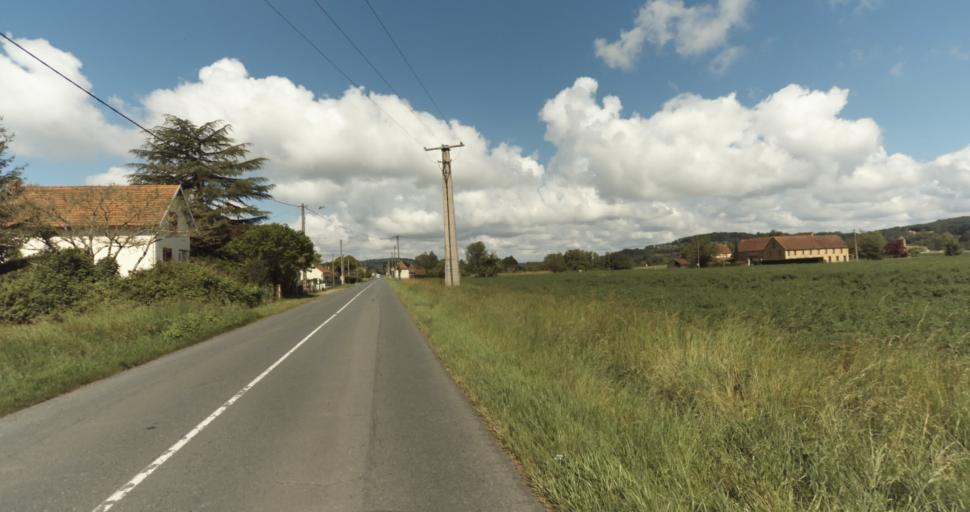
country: FR
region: Aquitaine
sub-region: Departement de la Dordogne
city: Le Bugue
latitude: 44.8441
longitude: 0.9227
